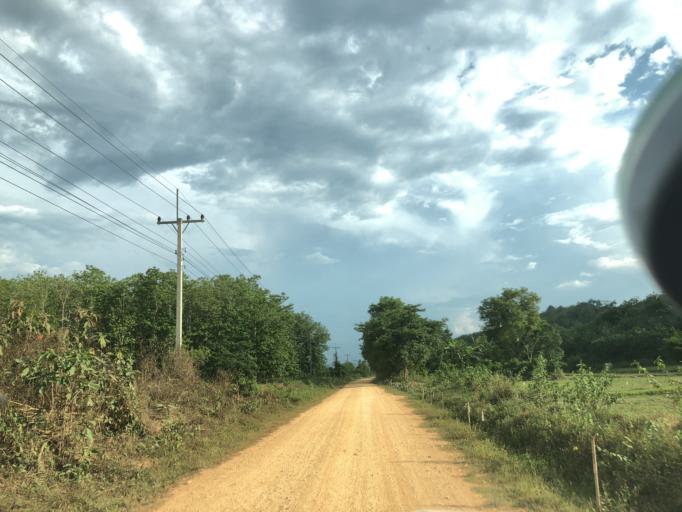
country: TH
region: Loei
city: Chiang Khan
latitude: 18.0030
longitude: 101.4202
